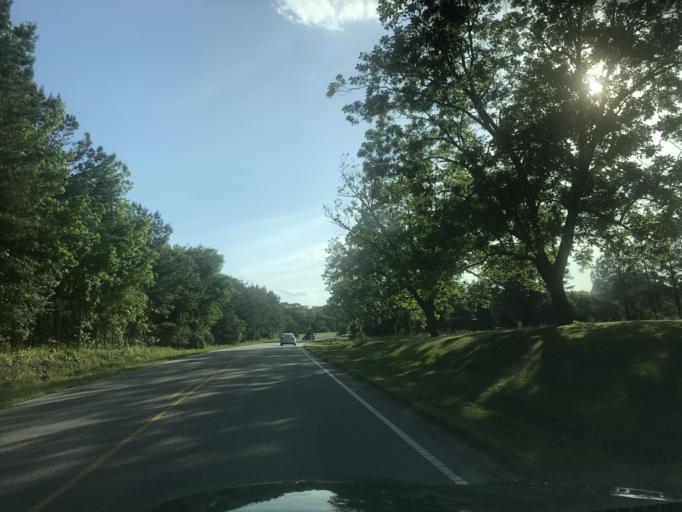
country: US
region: North Carolina
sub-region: Wake County
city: Knightdale
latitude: 35.7479
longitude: -78.4364
